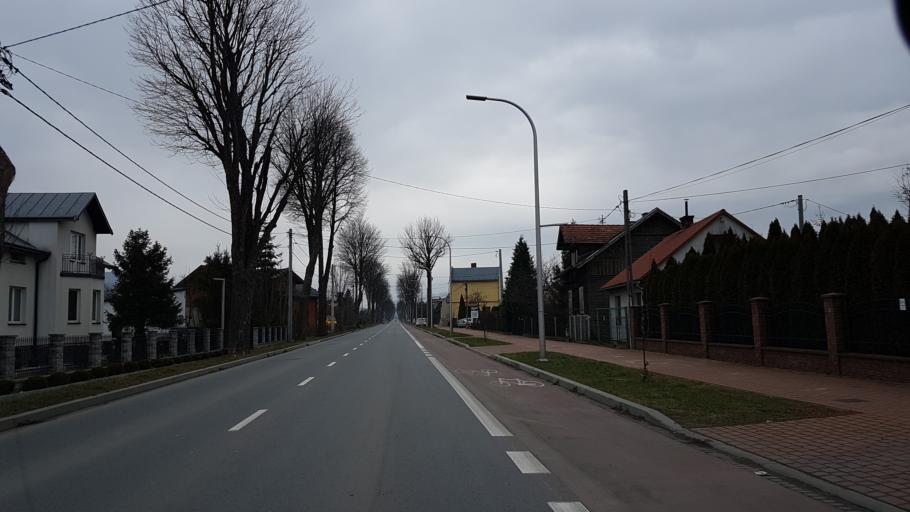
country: PL
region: Lesser Poland Voivodeship
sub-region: Powiat nowosadecki
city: Stary Sacz
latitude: 49.5546
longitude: 20.6389
